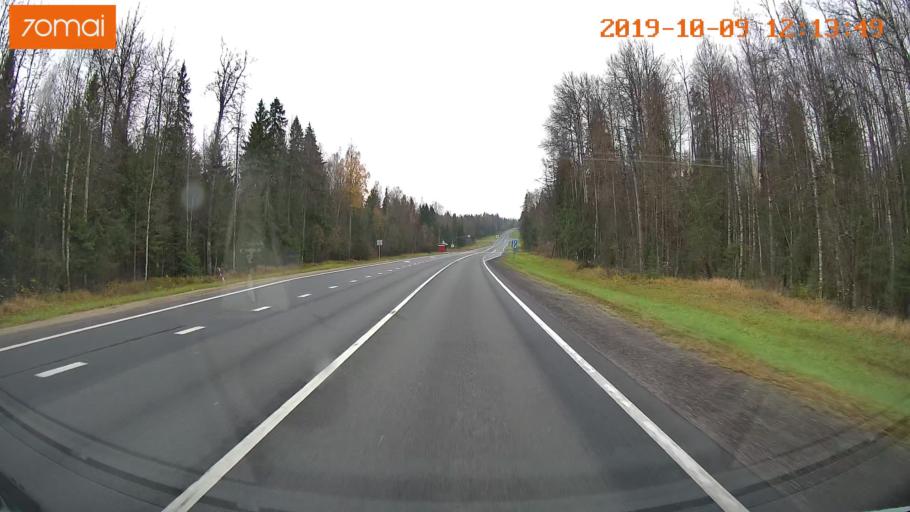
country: RU
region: Jaroslavl
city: Prechistoye
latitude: 58.5046
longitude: 40.3435
